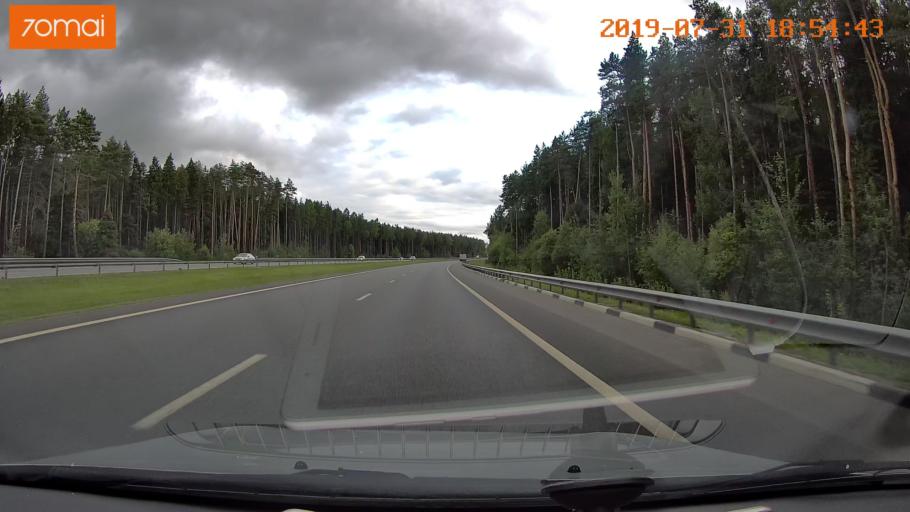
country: RU
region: Moskovskaya
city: Raduzhnyy
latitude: 55.1855
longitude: 38.6694
